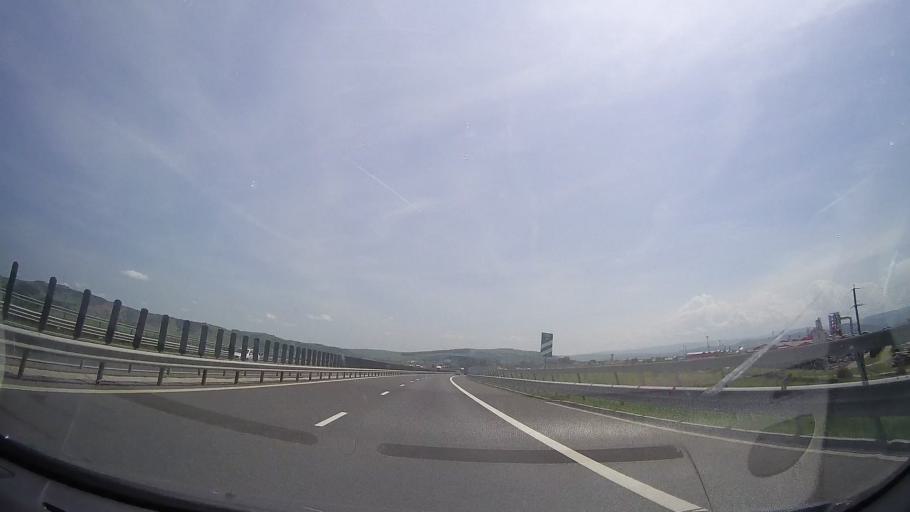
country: RO
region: Alba
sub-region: Municipiul Sebes
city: Lancram
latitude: 45.9794
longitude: 23.5487
